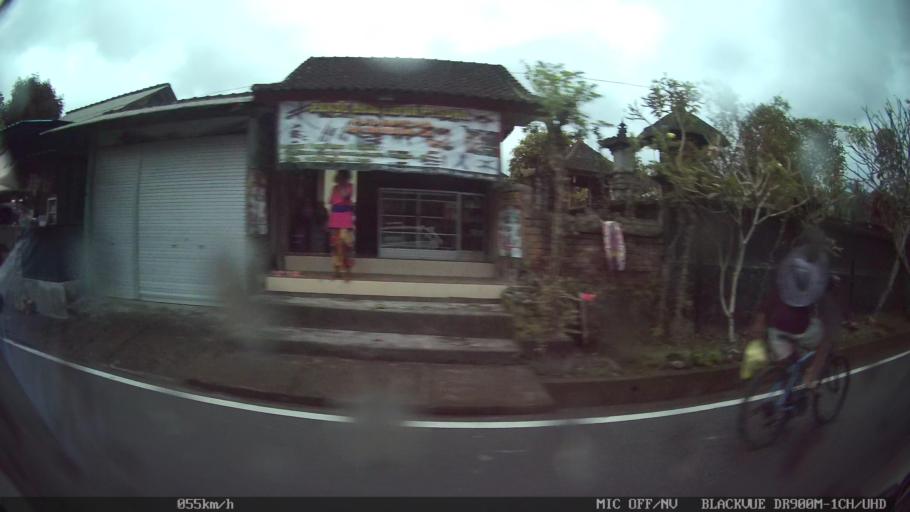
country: ID
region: Bali
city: Banjar Sayanbaleran
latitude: -8.5237
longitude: 115.1862
